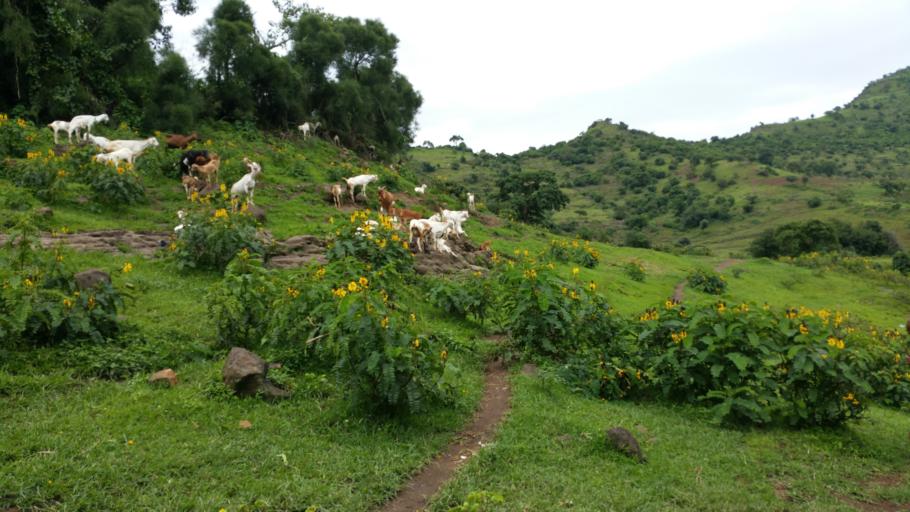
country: ET
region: Amhara
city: Bahir Dar
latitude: 11.4881
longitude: 37.5935
